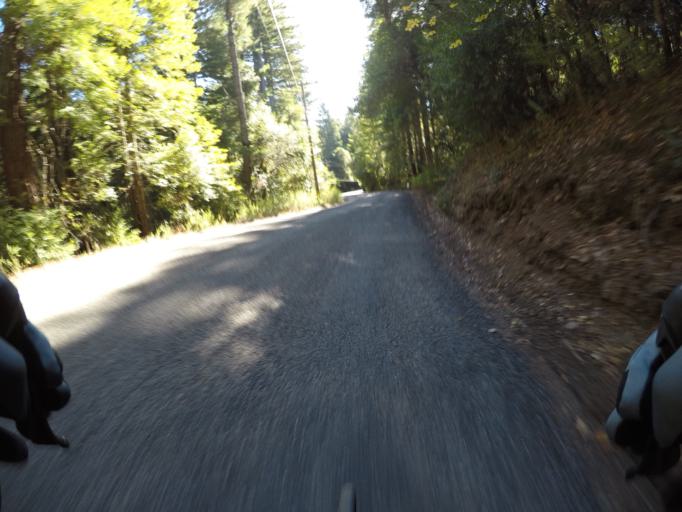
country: US
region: California
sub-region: Santa Cruz County
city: Lompico
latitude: 37.1142
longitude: -122.0207
